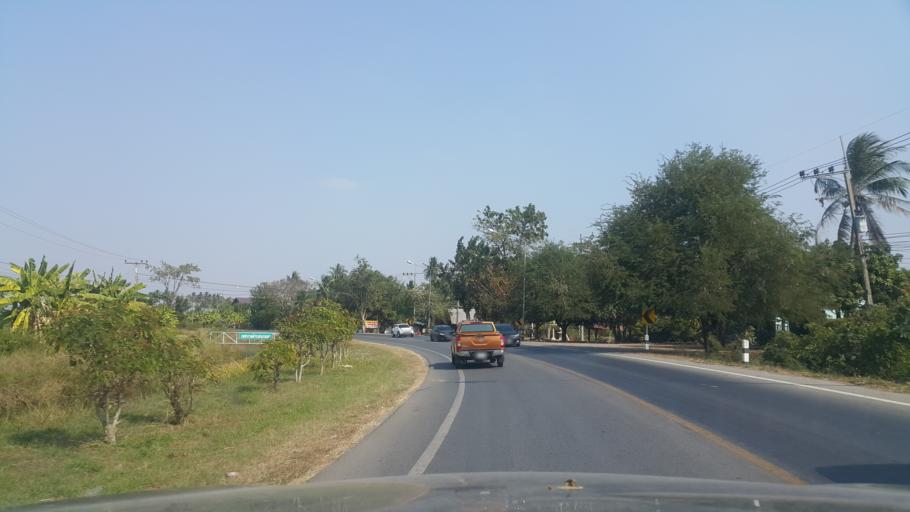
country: TH
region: Nakhon Ratchasima
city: Pak Thong Chai
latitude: 14.6926
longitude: 102.0239
